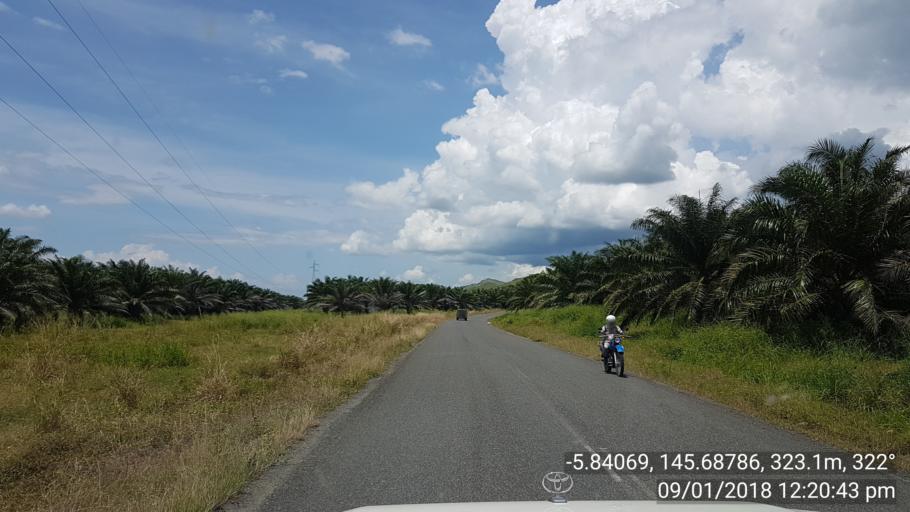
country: PG
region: Eastern Highlands
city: Goroka
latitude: -5.8413
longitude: 145.6885
